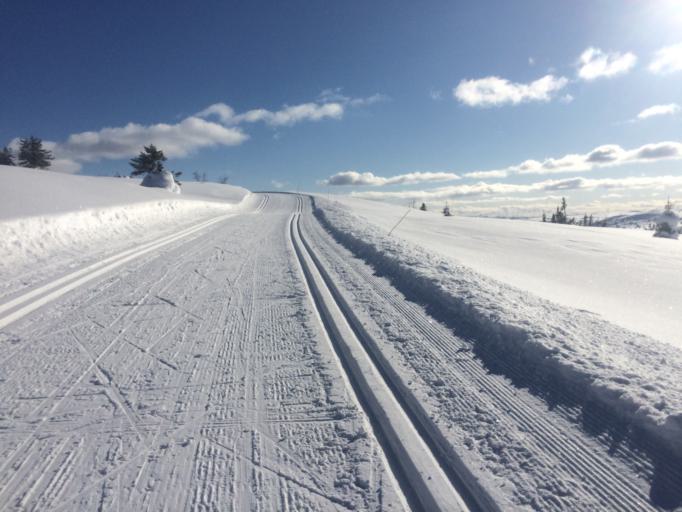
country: NO
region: Oppland
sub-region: Ringebu
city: Ringebu
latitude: 61.3735
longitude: 10.0601
